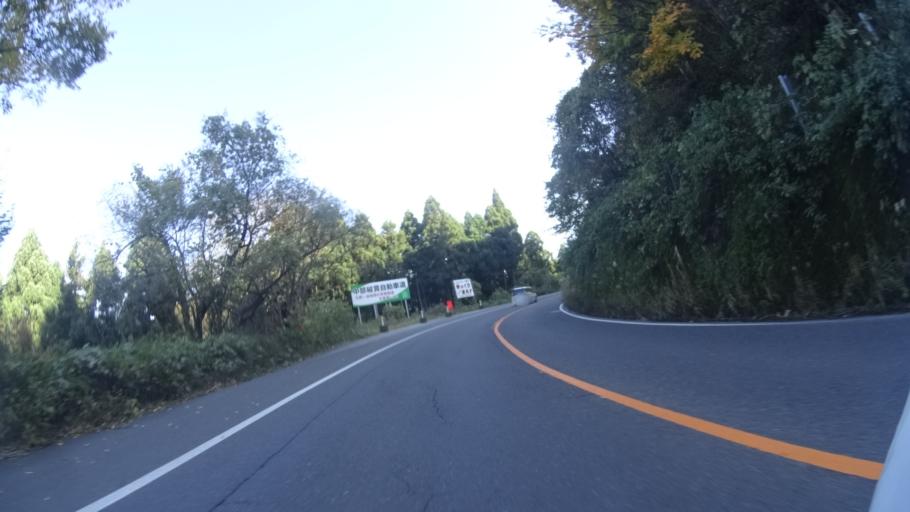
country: JP
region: Fukui
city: Ono
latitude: 35.9714
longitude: 136.5669
